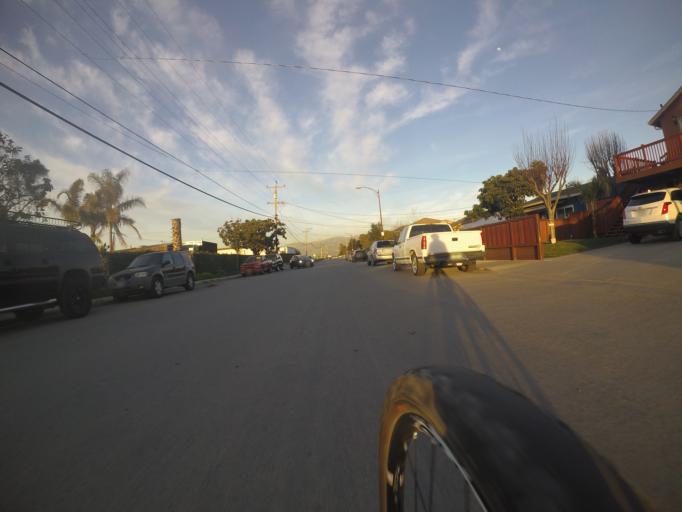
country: US
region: California
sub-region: Santa Clara County
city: Milpitas
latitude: 37.4308
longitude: -121.9696
